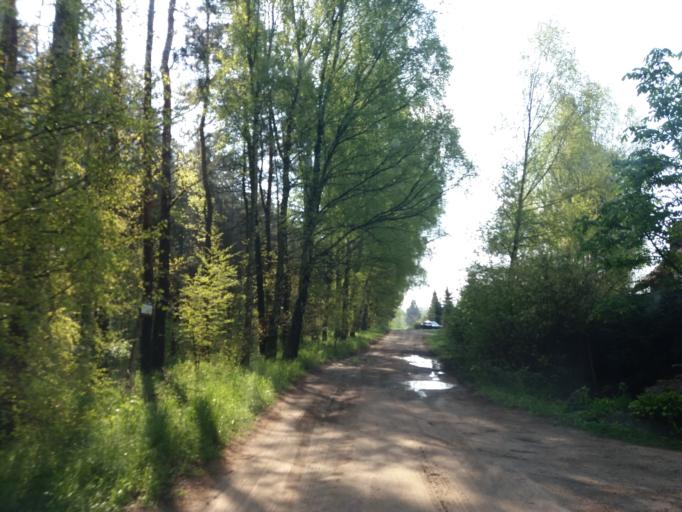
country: PL
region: West Pomeranian Voivodeship
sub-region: Powiat choszczenski
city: Drawno
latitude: 53.2123
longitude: 15.8339
